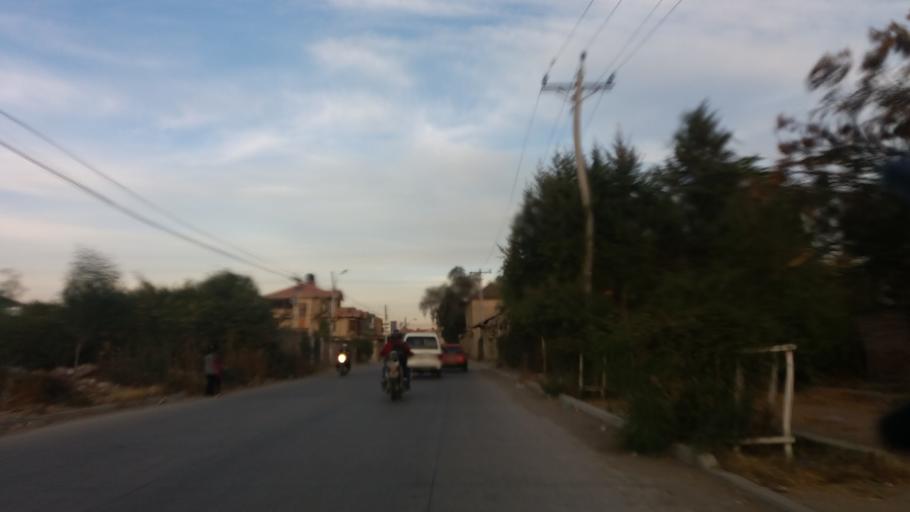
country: BO
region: Cochabamba
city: Cochabamba
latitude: -17.3738
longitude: -66.1997
